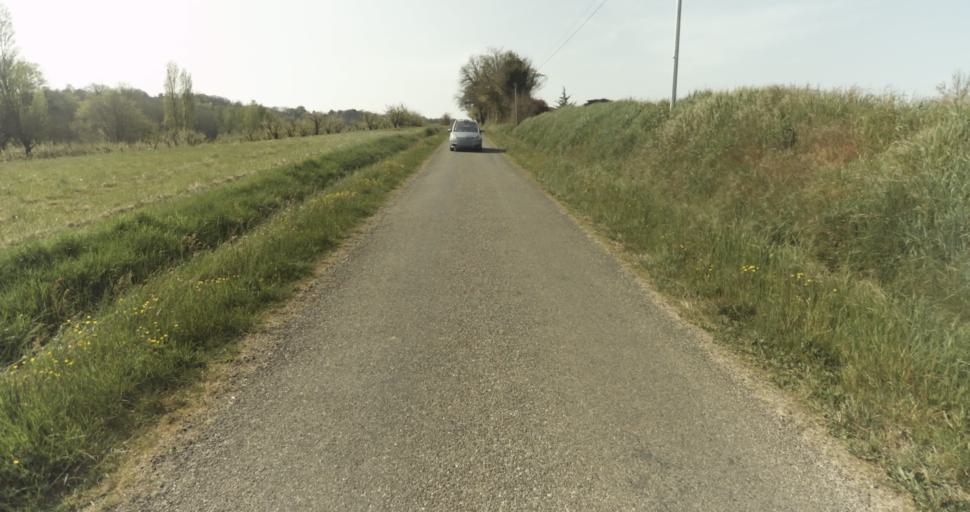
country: FR
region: Midi-Pyrenees
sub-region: Departement du Tarn-et-Garonne
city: Moissac
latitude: 44.1351
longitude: 1.1601
